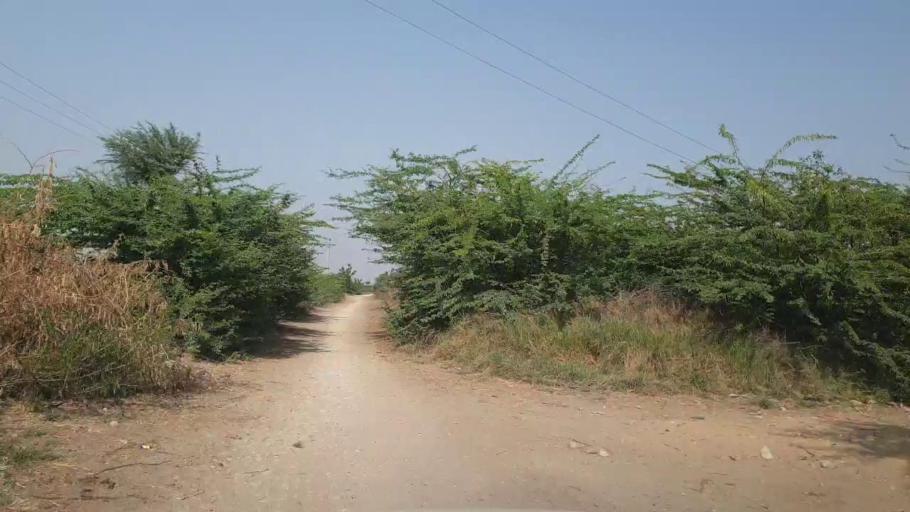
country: PK
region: Sindh
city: Dhoro Naro
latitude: 25.4816
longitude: 69.6066
